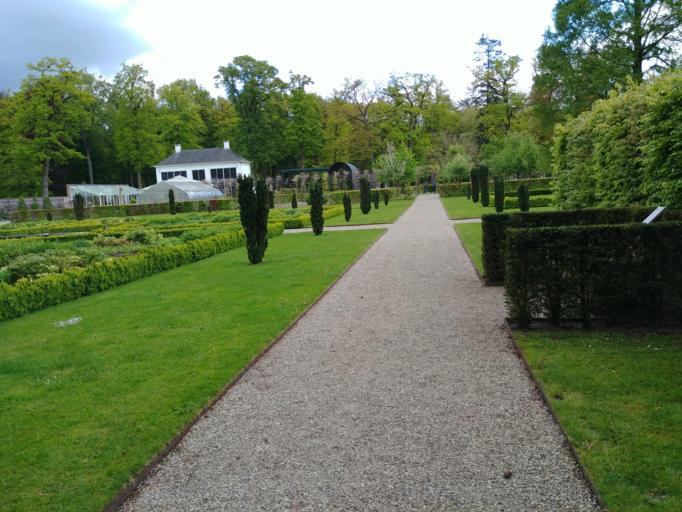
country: NL
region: Gelderland
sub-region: Gemeente Apeldoorn
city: Uddel
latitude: 52.2845
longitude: 5.7391
